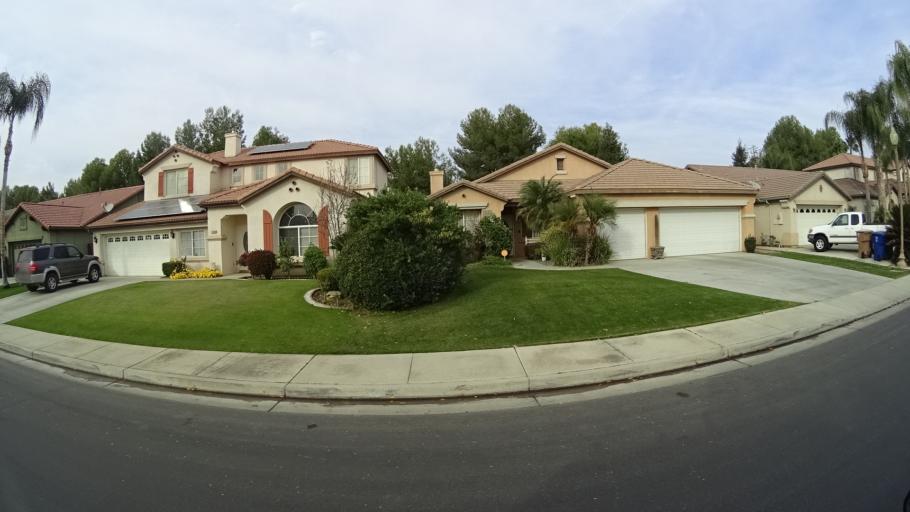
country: US
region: California
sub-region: Kern County
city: Rosedale
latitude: 35.3462
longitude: -119.1294
